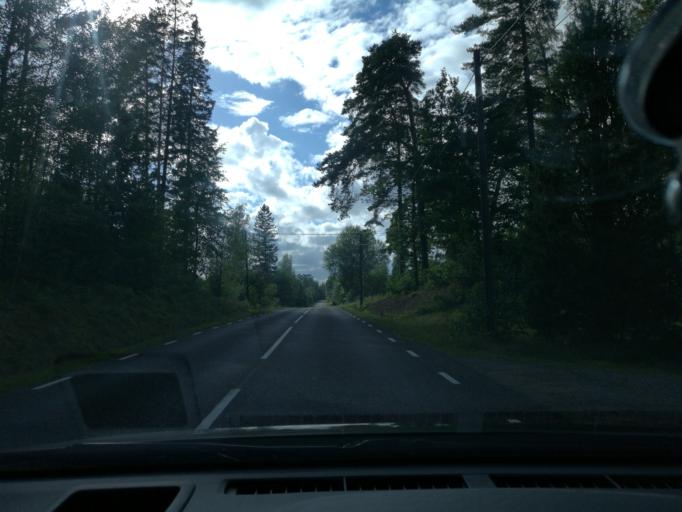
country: SE
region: Kronoberg
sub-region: Vaxjo Kommun
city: Braas
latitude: 57.0637
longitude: 15.0263
